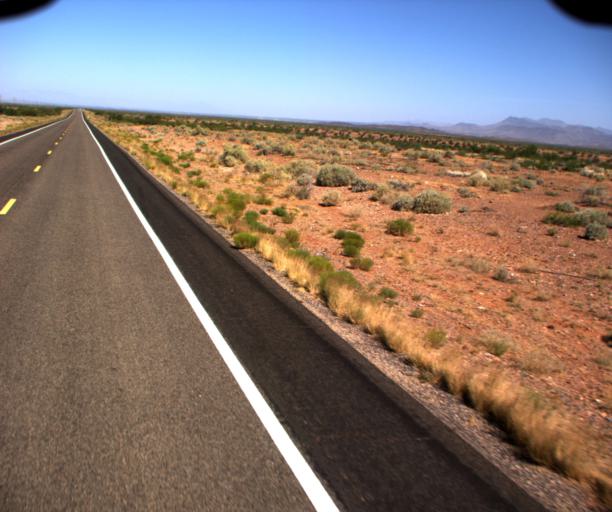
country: US
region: Arizona
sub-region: Graham County
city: Cactus Flat
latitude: 32.7675
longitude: -109.4663
